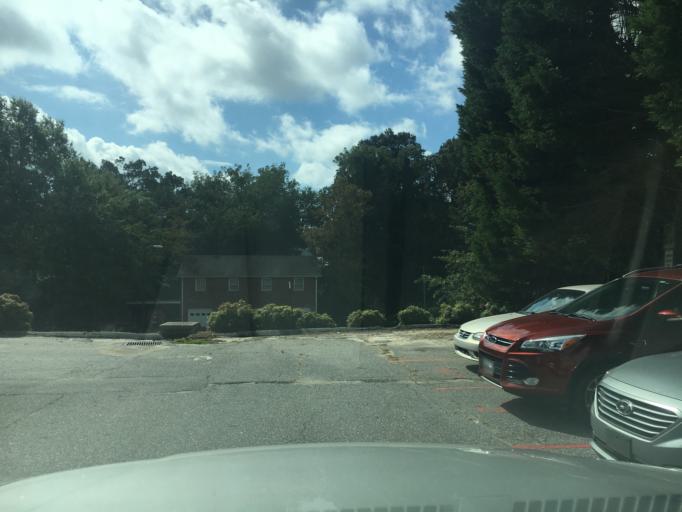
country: US
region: North Carolina
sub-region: Catawba County
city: Hickory
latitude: 35.7372
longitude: -81.3388
